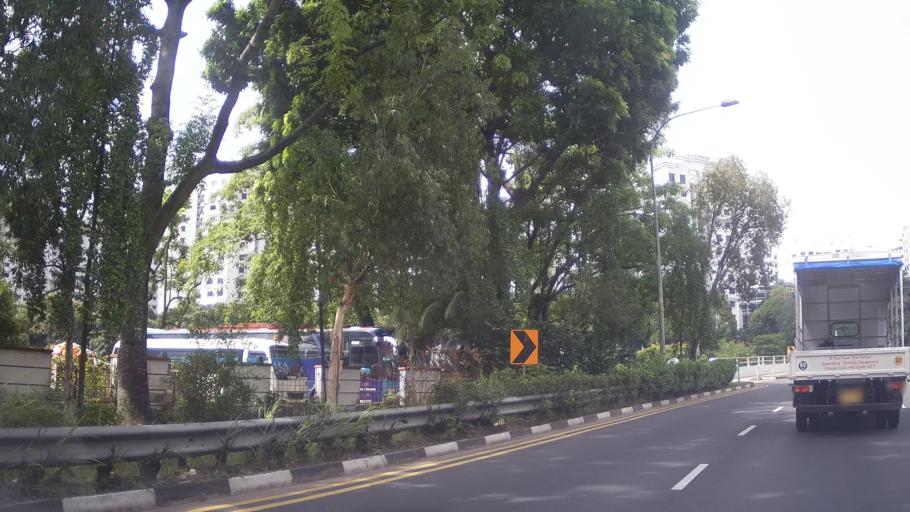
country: MY
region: Johor
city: Johor Bahru
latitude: 1.4061
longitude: 103.7463
